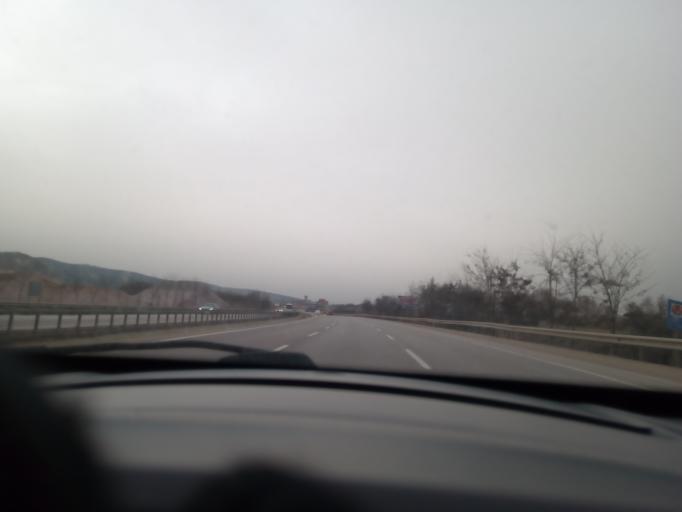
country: TR
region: Balikesir
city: Susurluk
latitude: 39.9630
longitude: 28.1702
